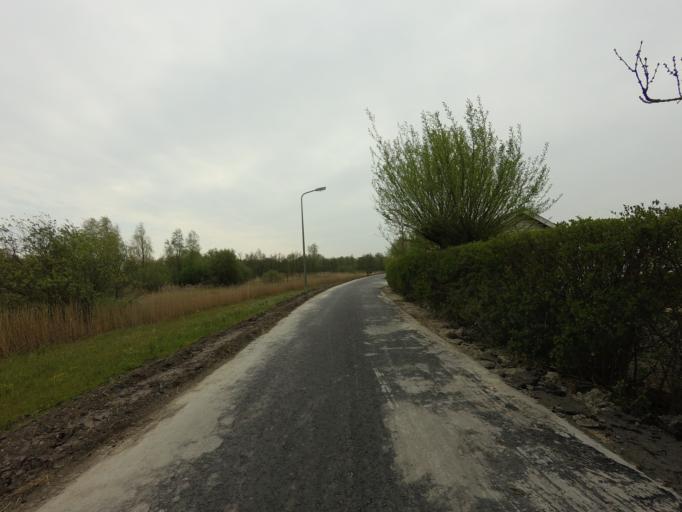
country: NL
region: North Holland
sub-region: Gemeente Diemen
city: Diemen
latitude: 52.3369
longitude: 4.9831
